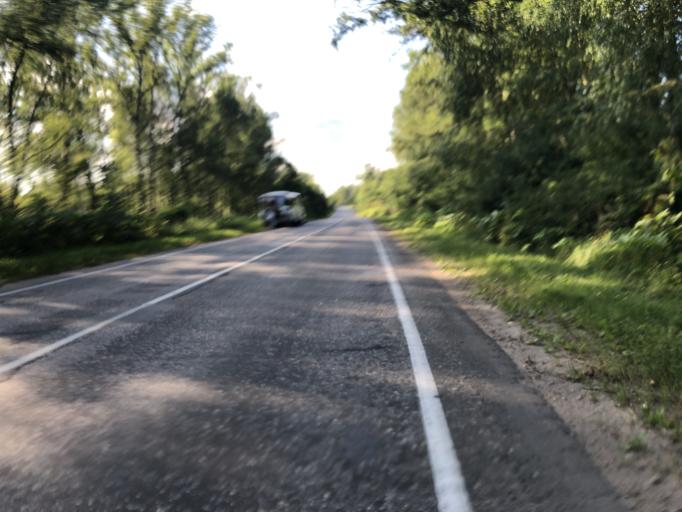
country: RU
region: Tverskaya
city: Rzhev
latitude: 56.2698
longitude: 34.2481
